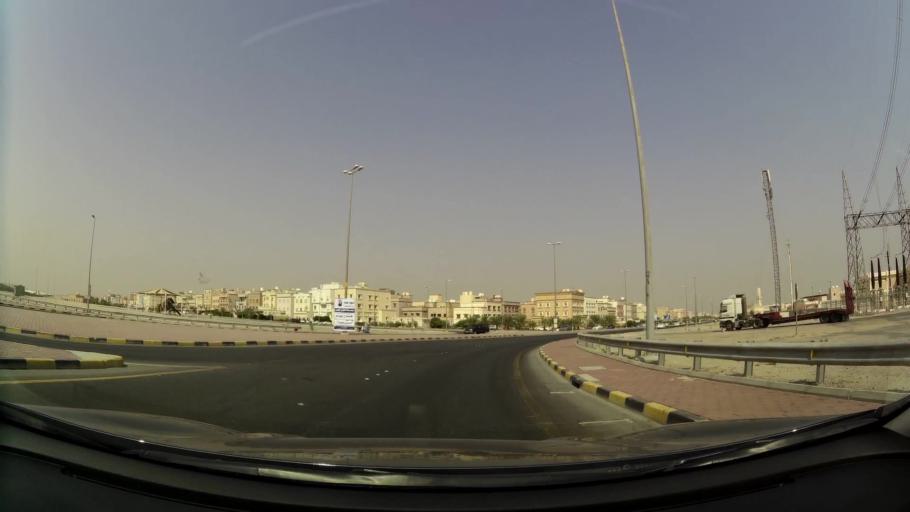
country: KW
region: Muhafazat al Jahra'
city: Al Jahra'
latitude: 29.2979
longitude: 47.7228
